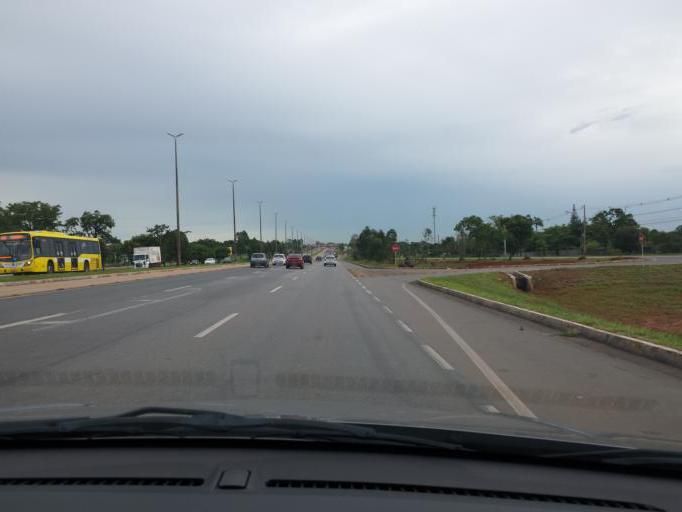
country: BR
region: Federal District
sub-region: Brasilia
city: Brasilia
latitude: -15.9208
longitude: -47.9738
